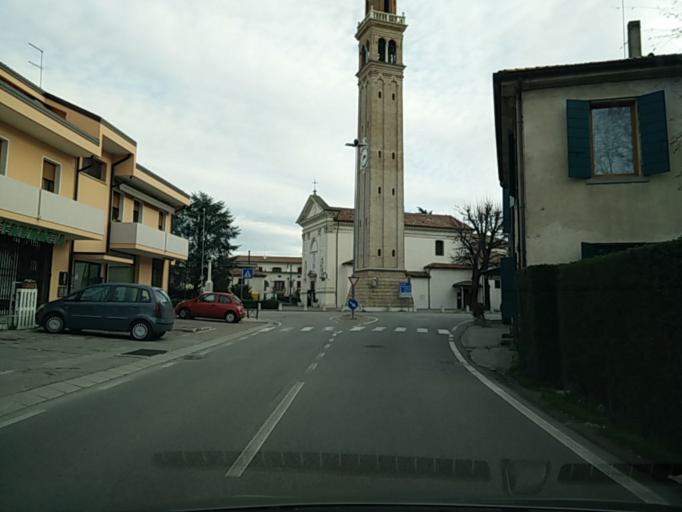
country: IT
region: Veneto
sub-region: Provincia di Treviso
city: Castagnole
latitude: 45.6885
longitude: 12.1833
